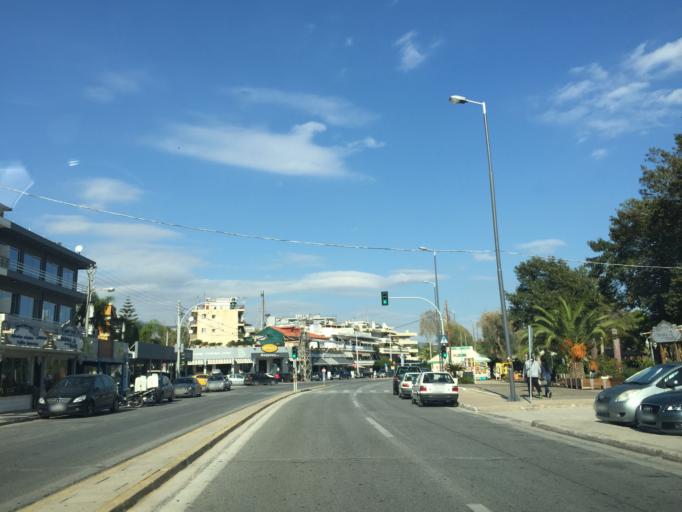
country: GR
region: Attica
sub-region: Nomarchia Anatolikis Attikis
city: Vari
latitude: 37.8177
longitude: 23.8019
